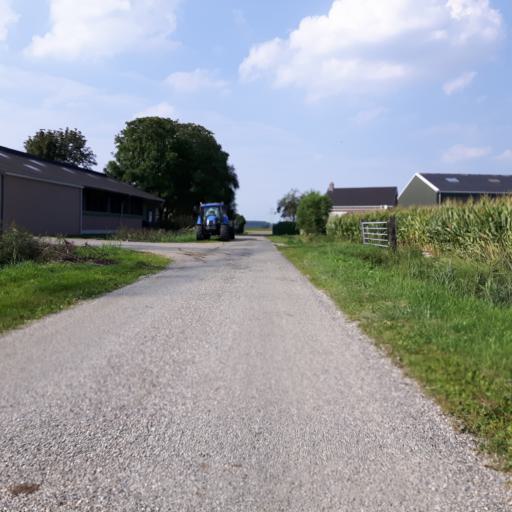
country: NL
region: Zeeland
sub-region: Gemeente Goes
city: Goes
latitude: 51.4630
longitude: 3.9443
